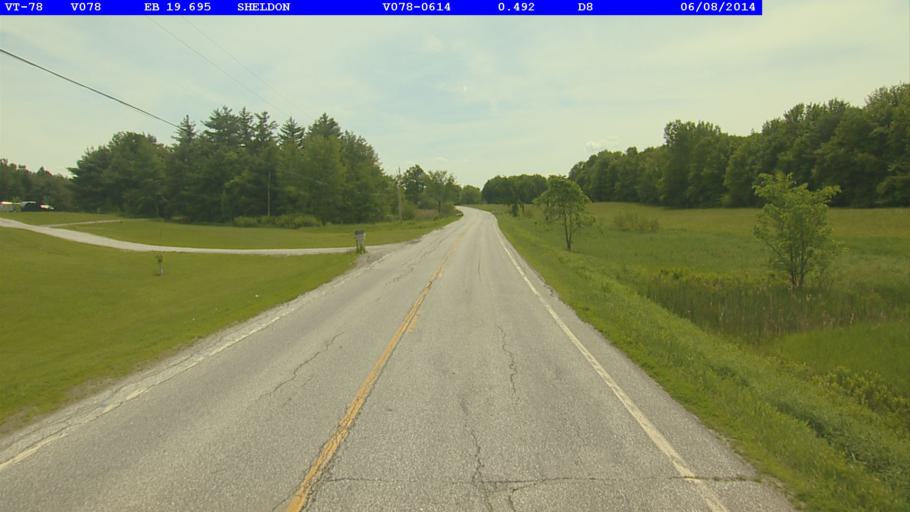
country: US
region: Vermont
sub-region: Franklin County
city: Enosburg Falls
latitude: 44.9186
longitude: -72.9626
